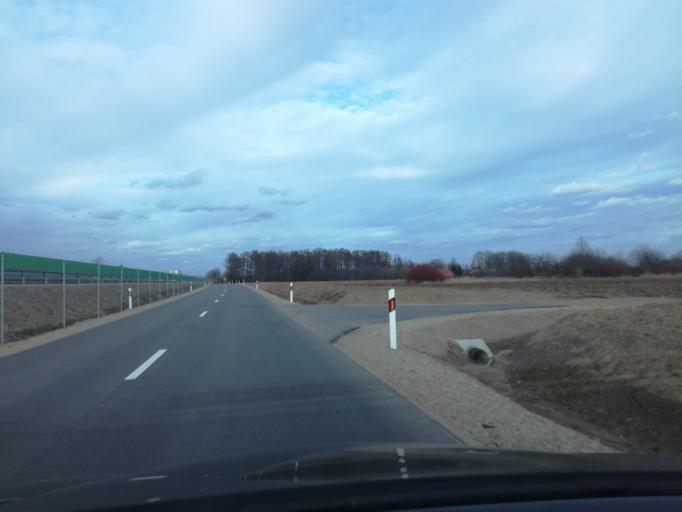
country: LT
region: Marijampoles apskritis
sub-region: Marijampole Municipality
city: Marijampole
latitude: 54.6021
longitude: 23.4038
